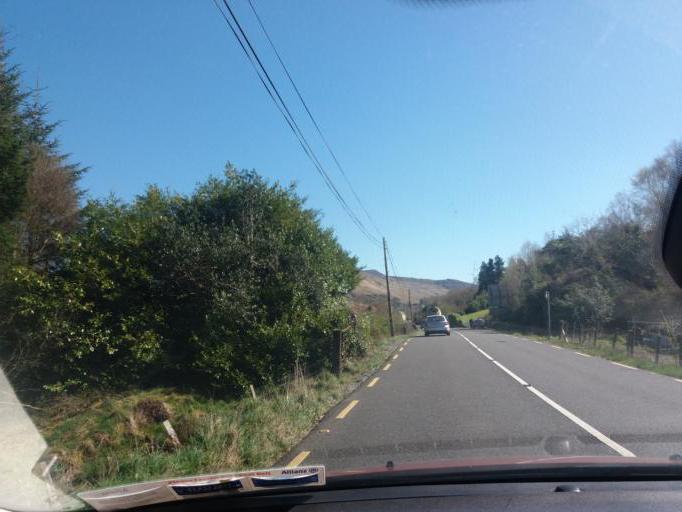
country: IE
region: Munster
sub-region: Ciarrai
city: Cill Airne
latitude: 51.9749
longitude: -9.3378
